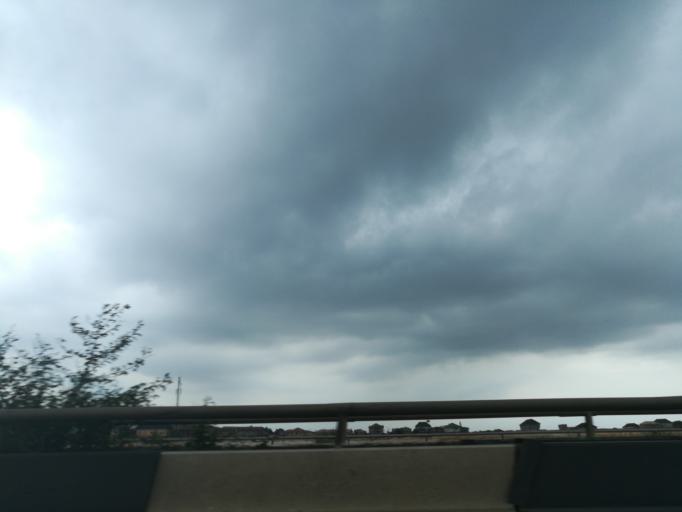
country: NG
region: Lagos
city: Somolu
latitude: 6.5390
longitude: 3.3999
